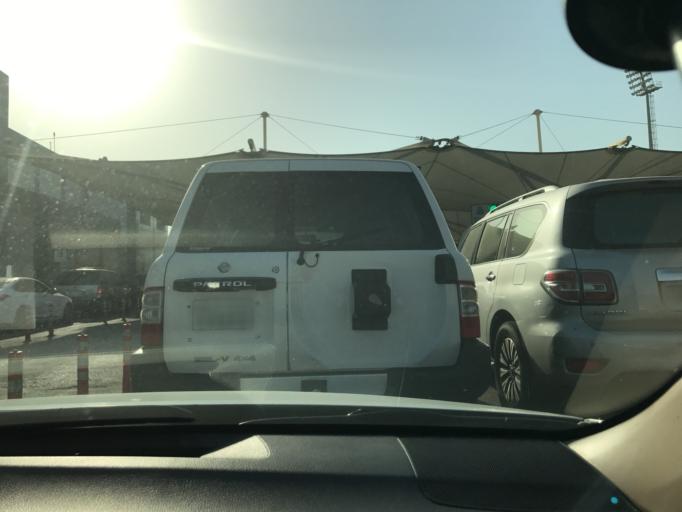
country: SA
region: Eastern Province
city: Khobar
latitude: 26.1850
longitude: 50.3232
